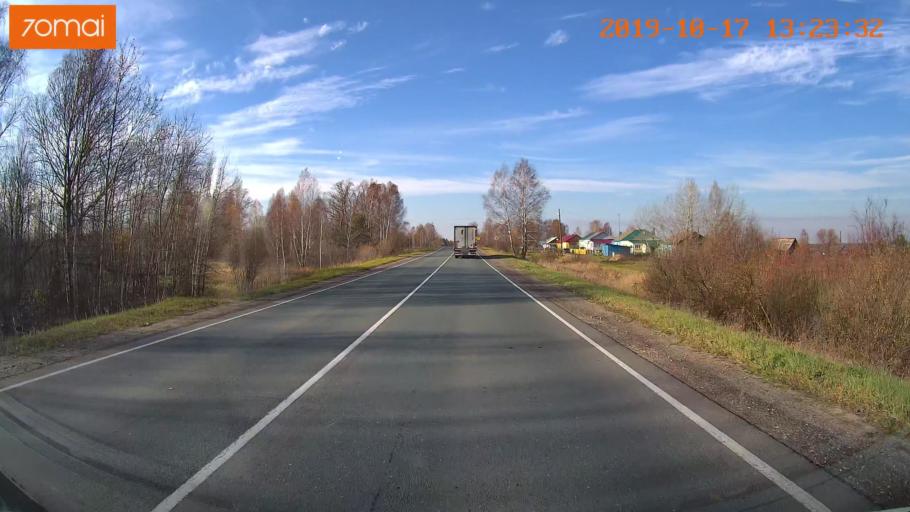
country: RU
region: Rjazan
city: Gus'-Zheleznyy
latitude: 55.0900
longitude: 40.9781
